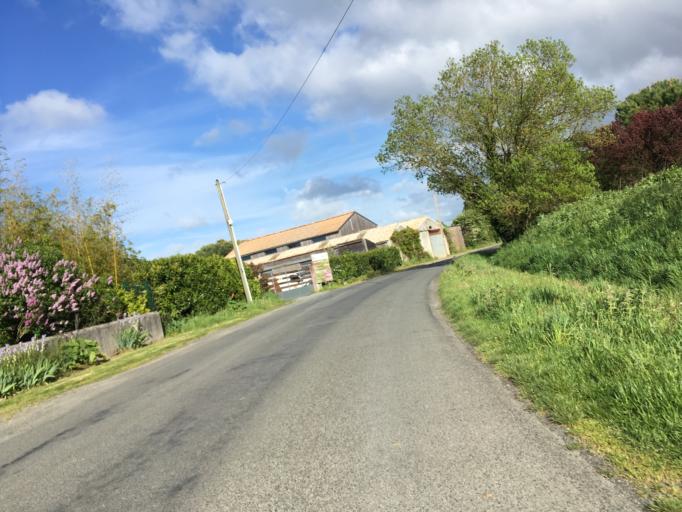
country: FR
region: Poitou-Charentes
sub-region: Departement de la Charente-Maritime
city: Verines
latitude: 46.1792
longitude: -0.9189
